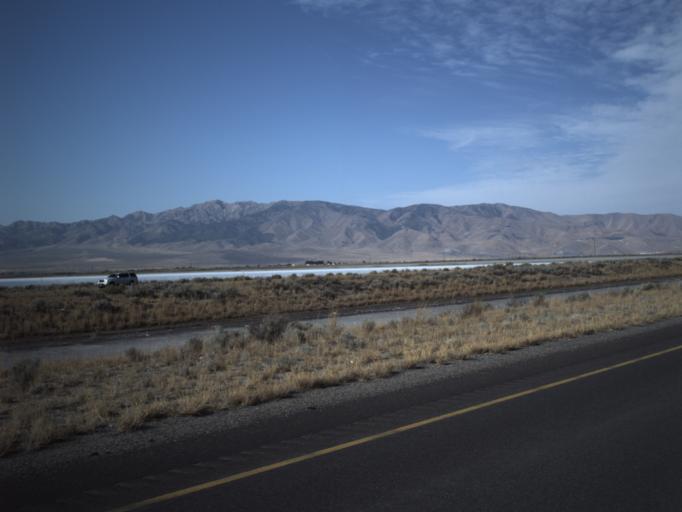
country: US
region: Utah
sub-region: Tooele County
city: Grantsville
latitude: 40.6754
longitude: -112.4002
